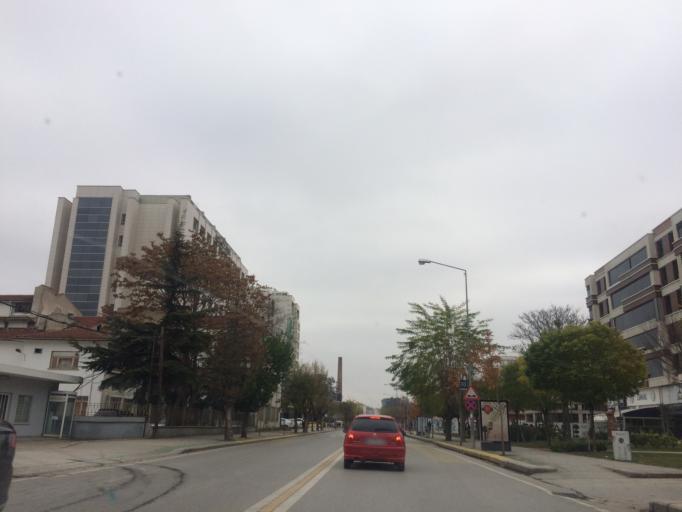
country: TR
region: Eskisehir
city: Eskisehir
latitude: 39.7835
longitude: 30.5049
